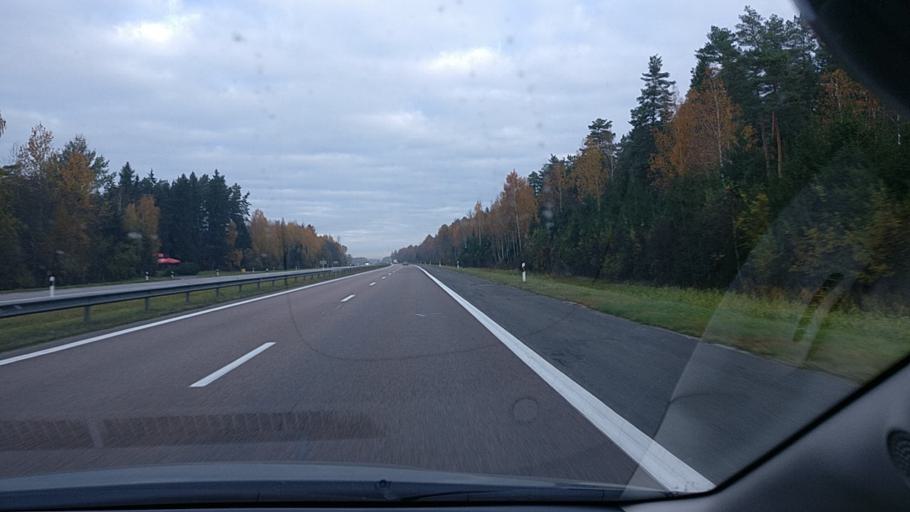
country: LT
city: Sirvintos
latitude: 54.9702
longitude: 24.9483
